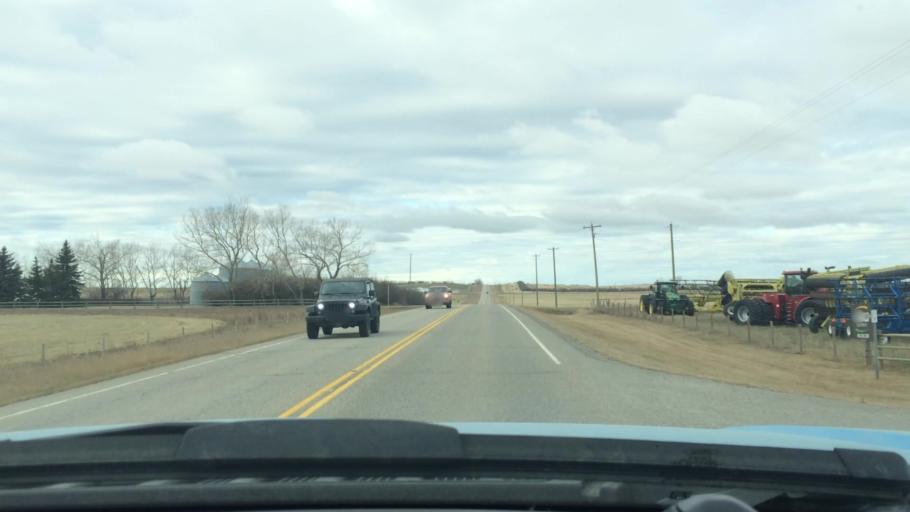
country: CA
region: Alberta
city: Airdrie
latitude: 51.2126
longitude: -114.0350
